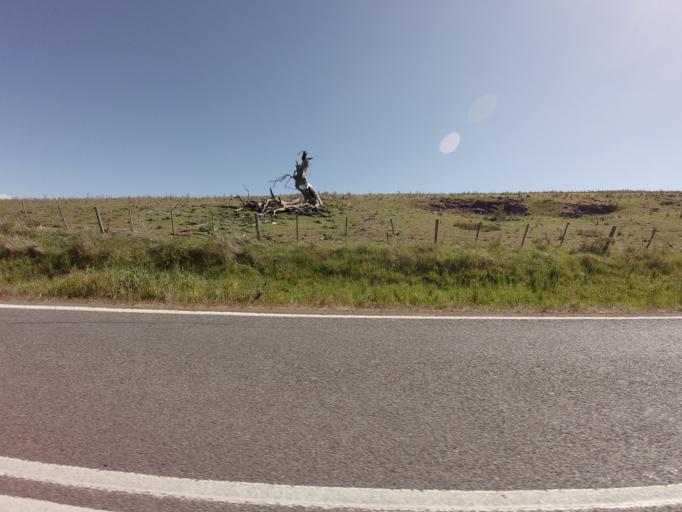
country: AU
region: Tasmania
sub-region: Derwent Valley
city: New Norfolk
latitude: -42.6421
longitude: 146.9194
